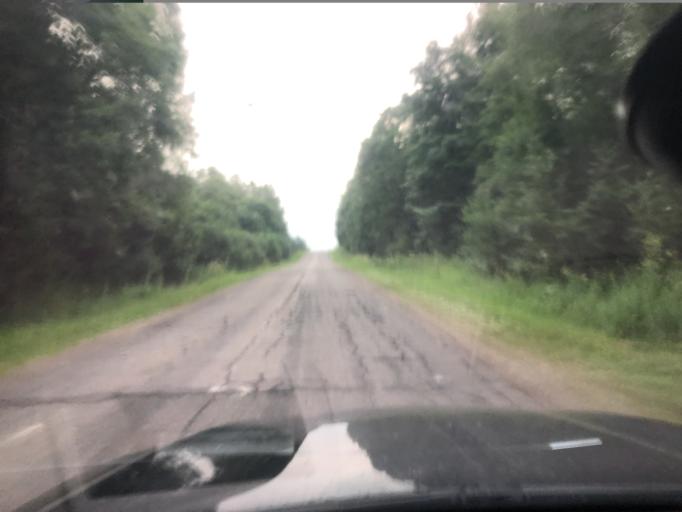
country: RU
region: Jaroslavl
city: Petrovsk
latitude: 56.9978
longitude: 39.0996
